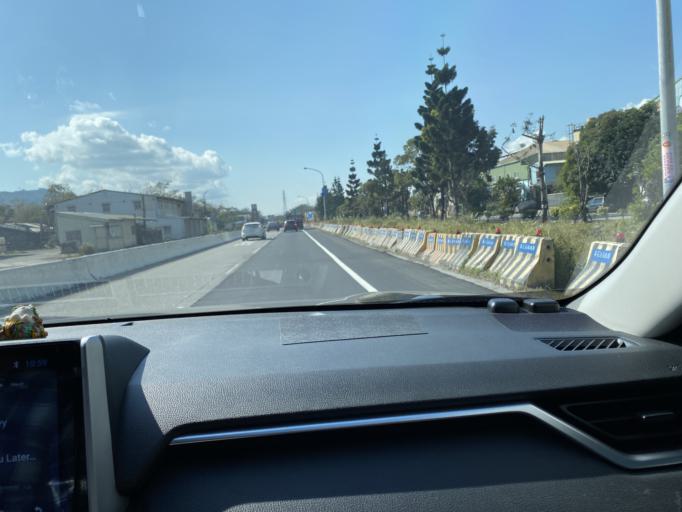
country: TW
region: Taiwan
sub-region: Hualien
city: Hualian
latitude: 23.9297
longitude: 121.5933
